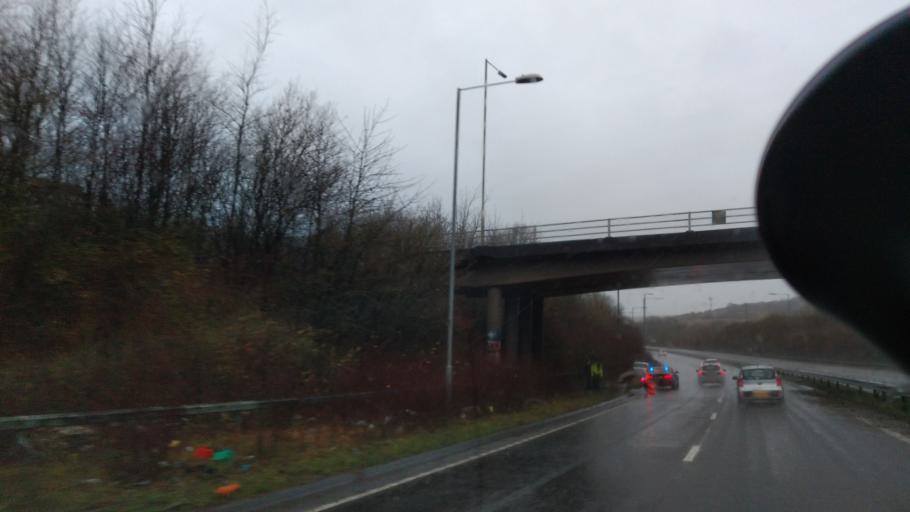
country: GB
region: England
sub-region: Brighton and Hove
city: Hove
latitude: 50.8693
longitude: -0.1515
